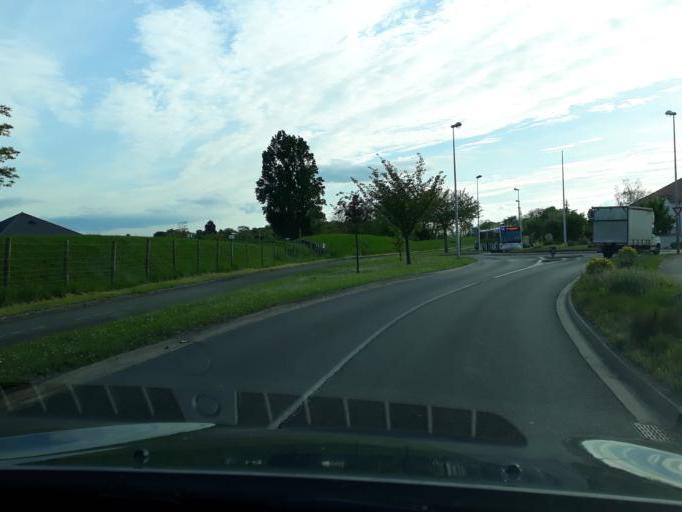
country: FR
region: Centre
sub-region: Departement du Loiret
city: Ingre
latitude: 47.9224
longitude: 1.8412
